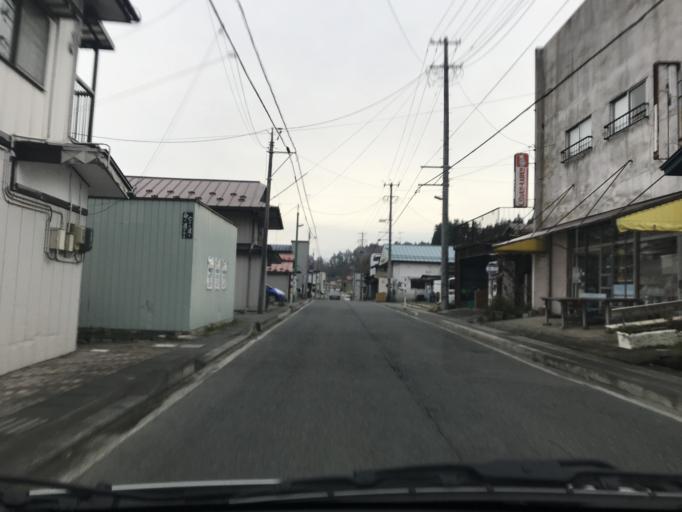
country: JP
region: Iwate
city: Kitakami
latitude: 39.2885
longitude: 141.2623
